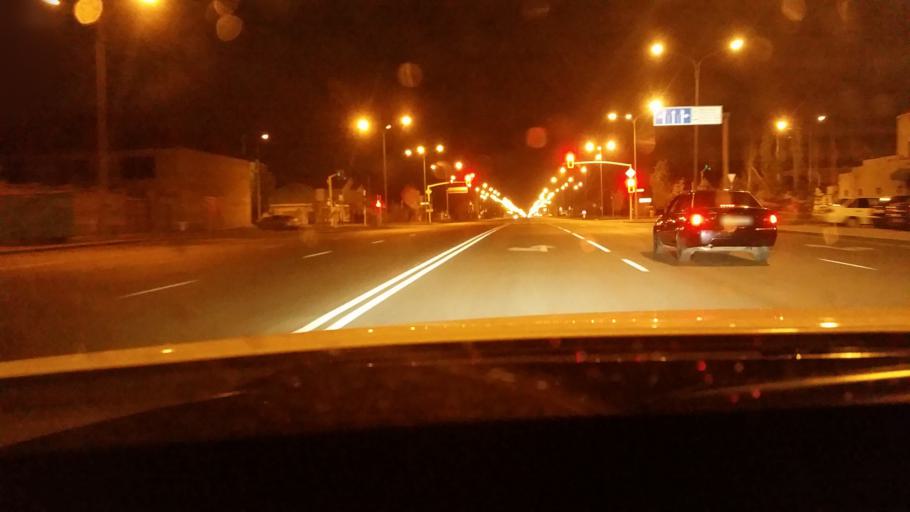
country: KZ
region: Astana Qalasy
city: Astana
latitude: 51.1332
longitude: 71.4943
